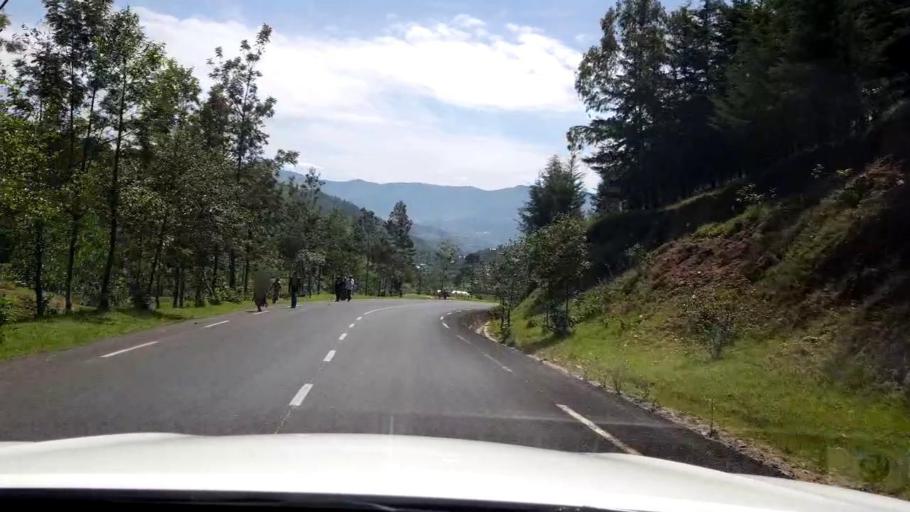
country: RW
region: Southern Province
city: Gitarama
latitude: -1.9183
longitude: 29.6362
